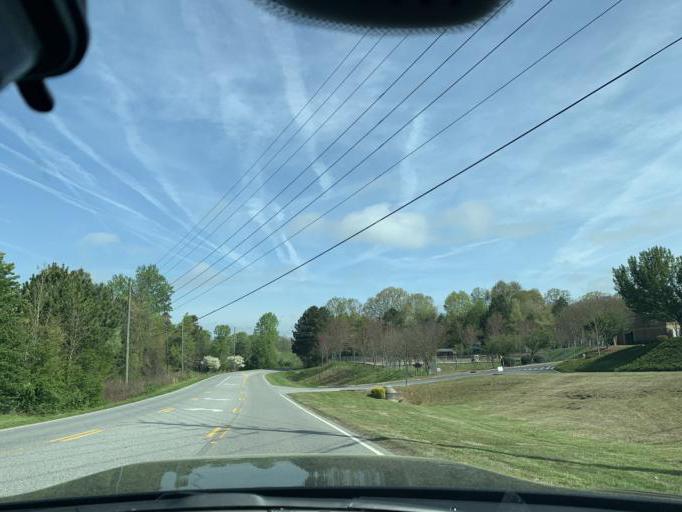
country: US
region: Georgia
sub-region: Forsyth County
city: Cumming
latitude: 34.2381
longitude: -84.0877
